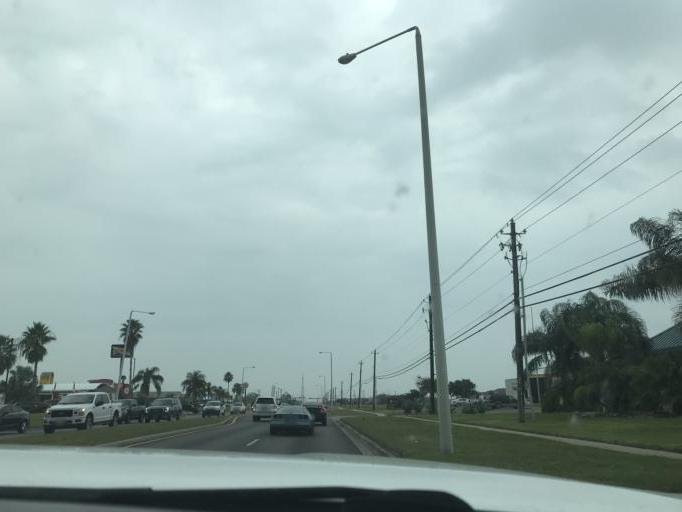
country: US
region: Texas
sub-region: Nueces County
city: Corpus Christi
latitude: 27.6778
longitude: -97.3684
